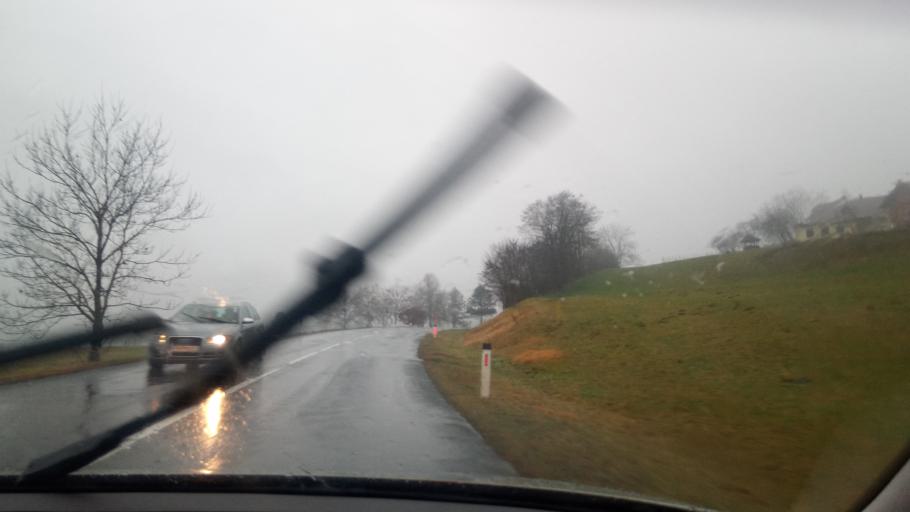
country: AT
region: Carinthia
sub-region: Politischer Bezirk Klagenfurt Land
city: Keutschach am See
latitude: 46.5892
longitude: 14.1761
